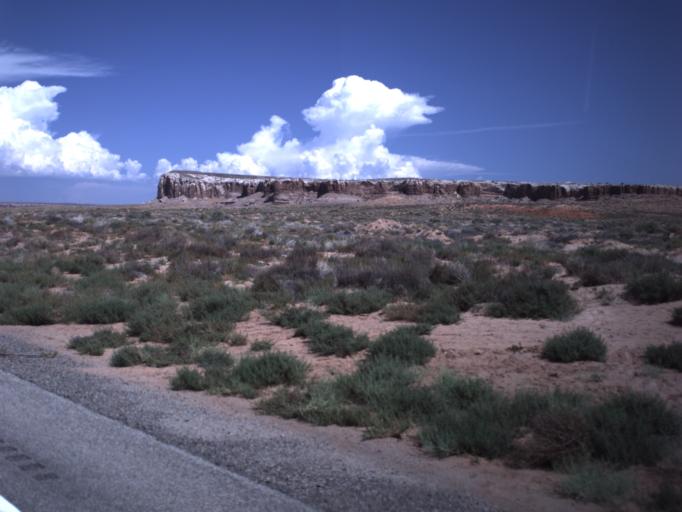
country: US
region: Utah
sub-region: San Juan County
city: Blanding
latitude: 37.2124
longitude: -109.6113
